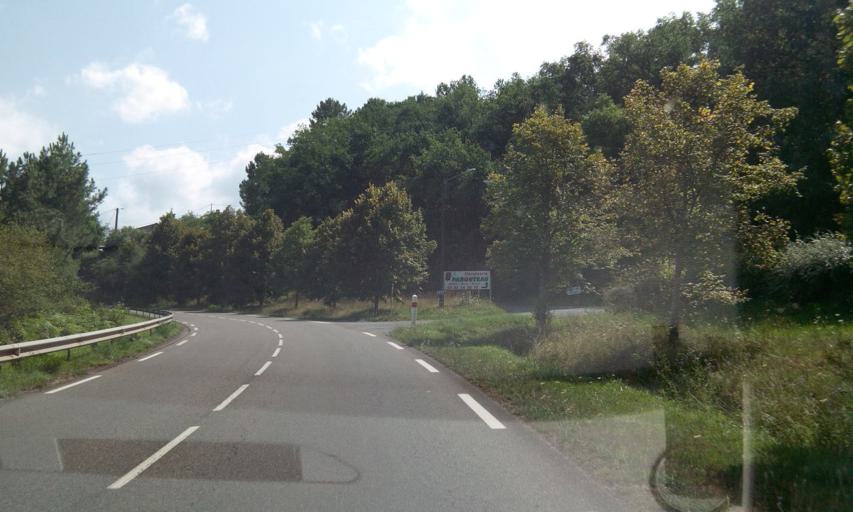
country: FR
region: Limousin
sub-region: Departement de la Correze
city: Brive-la-Gaillarde
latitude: 45.1289
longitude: 1.5541
